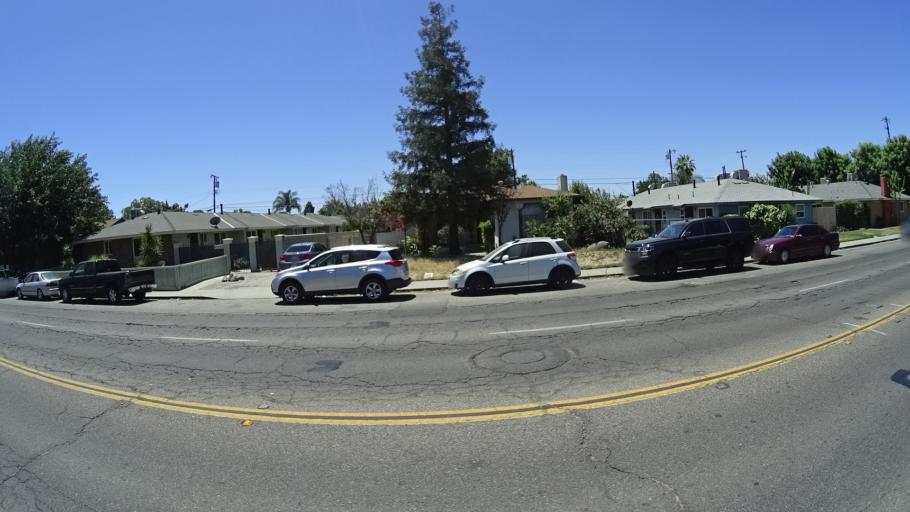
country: US
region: California
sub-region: Fresno County
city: Fresno
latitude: 36.7723
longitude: -119.7701
